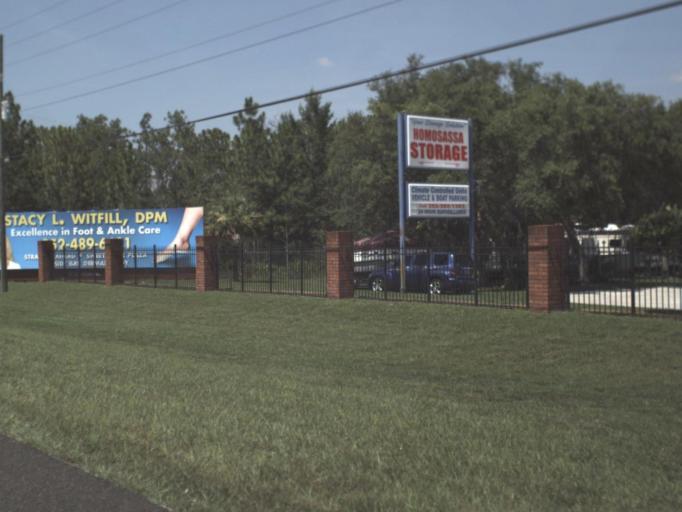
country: US
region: Florida
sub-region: Citrus County
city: Sugarmill Woods
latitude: 28.7342
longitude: -82.5527
